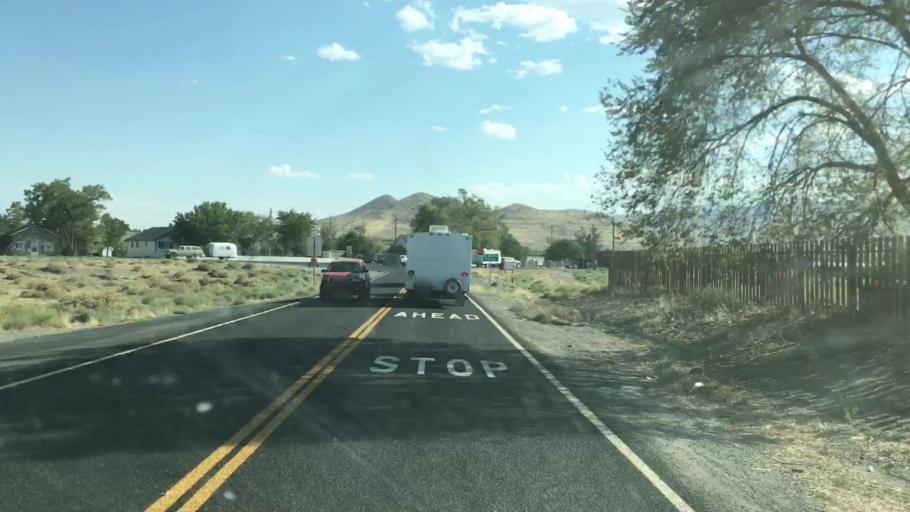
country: US
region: Nevada
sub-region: Lyon County
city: Fernley
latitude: 39.6318
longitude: -119.2906
